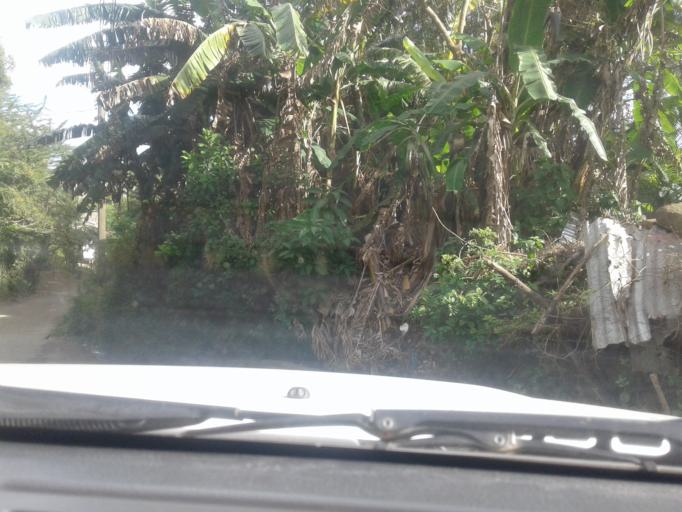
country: NI
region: Carazo
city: Diriamba
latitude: 11.8519
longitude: -86.2388
